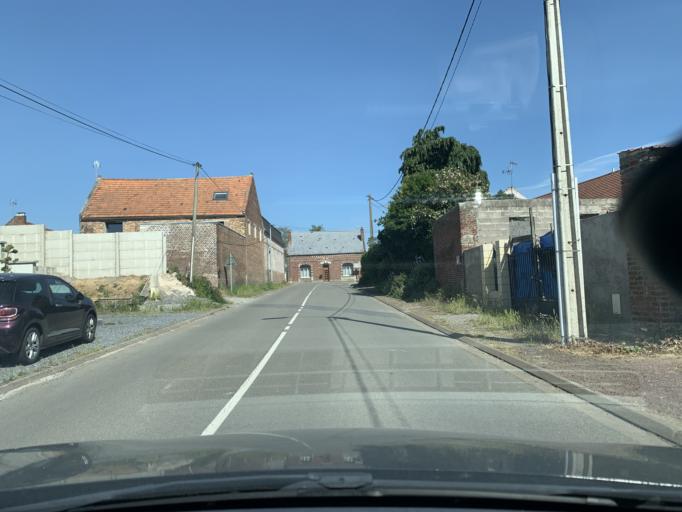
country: FR
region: Nord-Pas-de-Calais
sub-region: Departement du Nord
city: Fontaine-Notre-Dame
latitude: 50.1488
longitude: 3.1665
